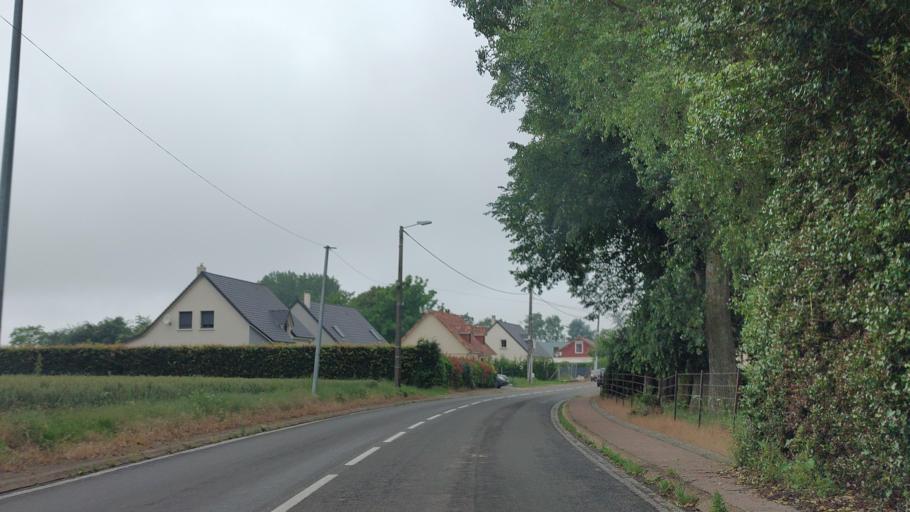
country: FR
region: Picardie
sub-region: Departement de la Somme
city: Bethencourt-sur-Mer
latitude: 50.0730
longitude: 1.5055
